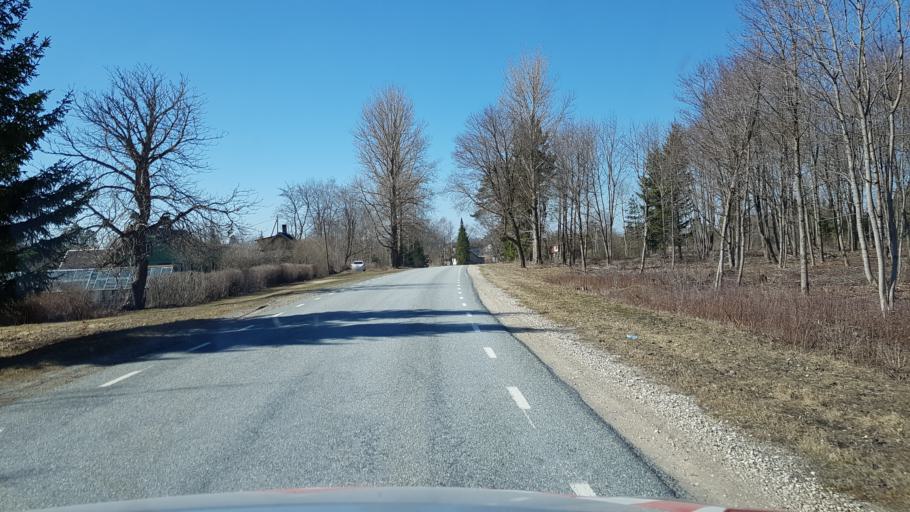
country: EE
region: Laeaene-Virumaa
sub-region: Vaeike-Maarja vald
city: Vaike-Maarja
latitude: 59.1260
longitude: 26.2778
